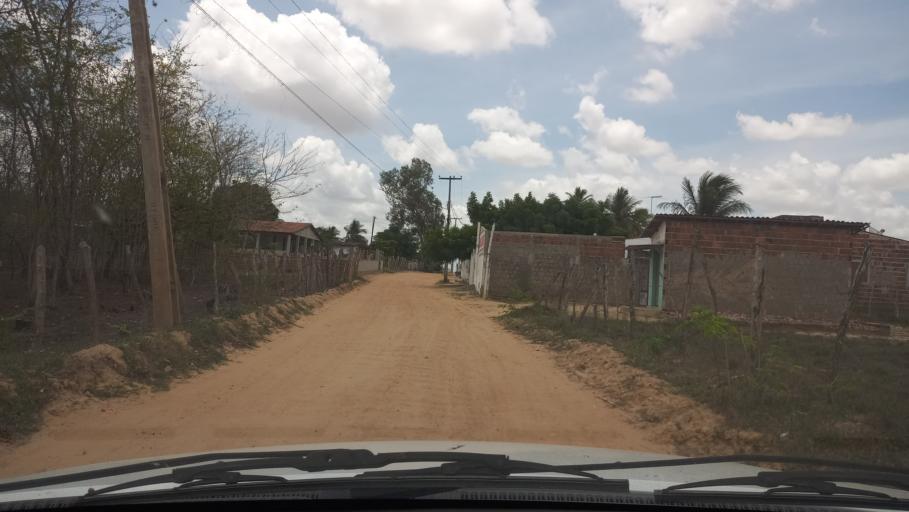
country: BR
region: Rio Grande do Norte
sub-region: Brejinho
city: Brejinho
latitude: -6.2938
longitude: -35.3443
